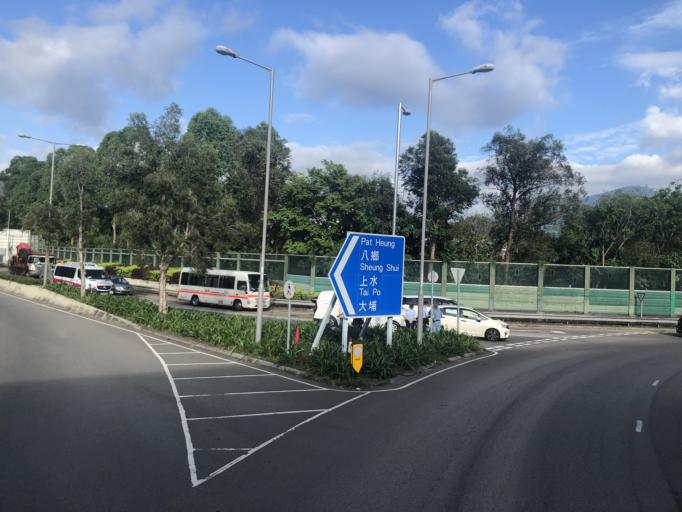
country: HK
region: Yuen Long
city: Yuen Long Kau Hui
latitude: 22.4406
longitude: 114.0597
